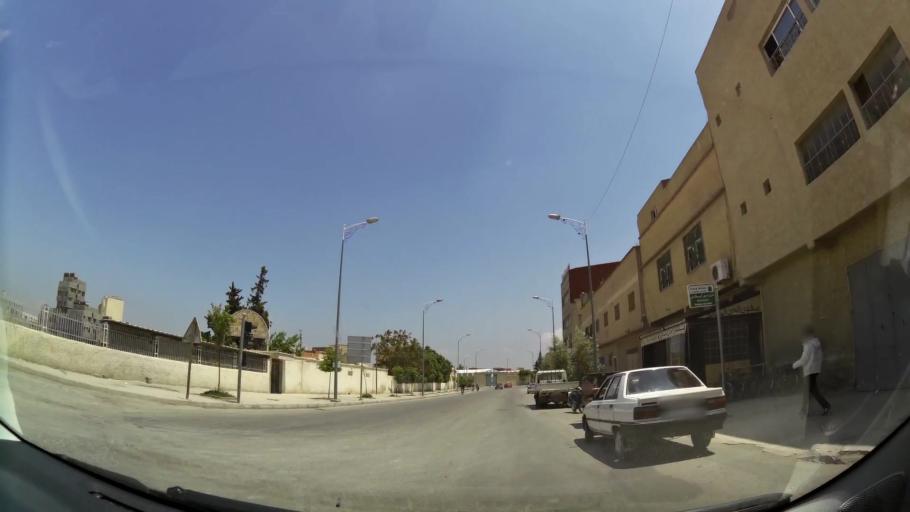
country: MA
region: Oriental
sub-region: Oujda-Angad
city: Oujda
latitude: 34.7014
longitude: -1.8966
